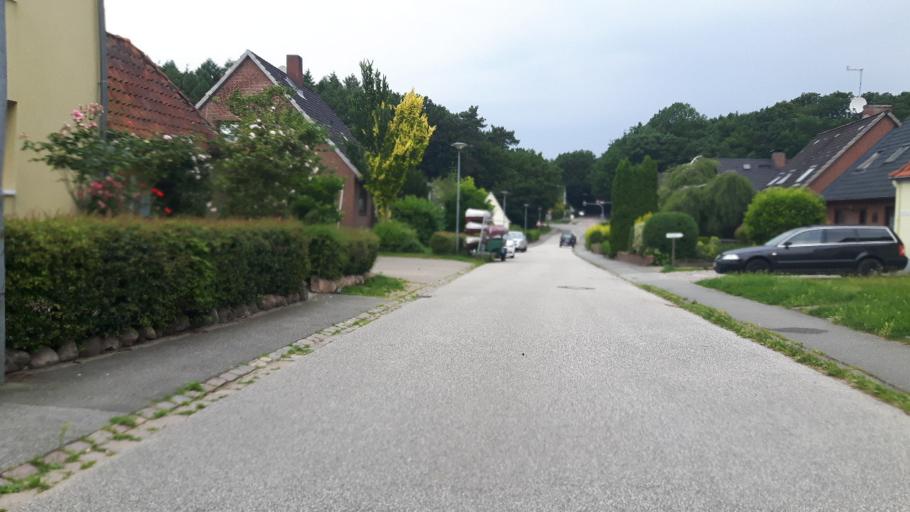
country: DE
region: Schleswig-Holstein
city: Ratekau
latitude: 53.9128
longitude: 10.7877
